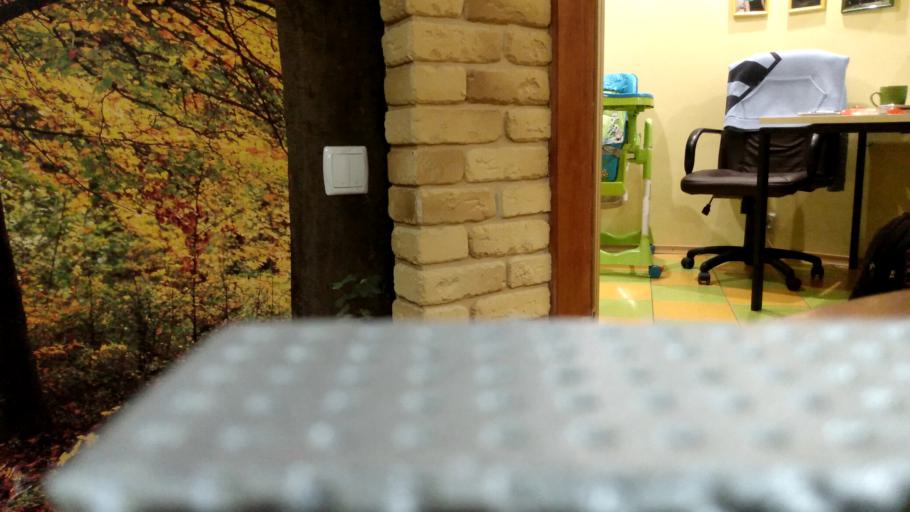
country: RU
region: Republic of Karelia
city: Pudozh
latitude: 61.9385
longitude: 37.6217
